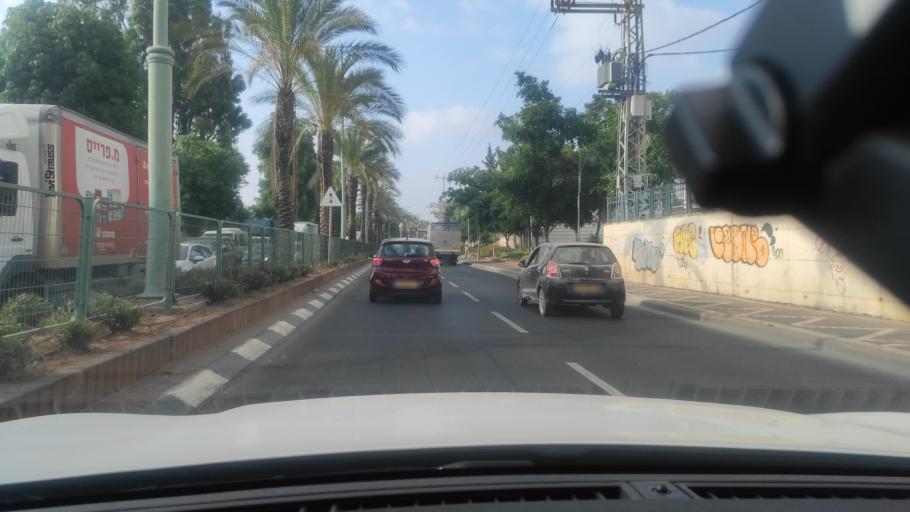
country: IL
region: Central District
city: Petah Tiqwa
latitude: 32.0939
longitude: 34.9019
